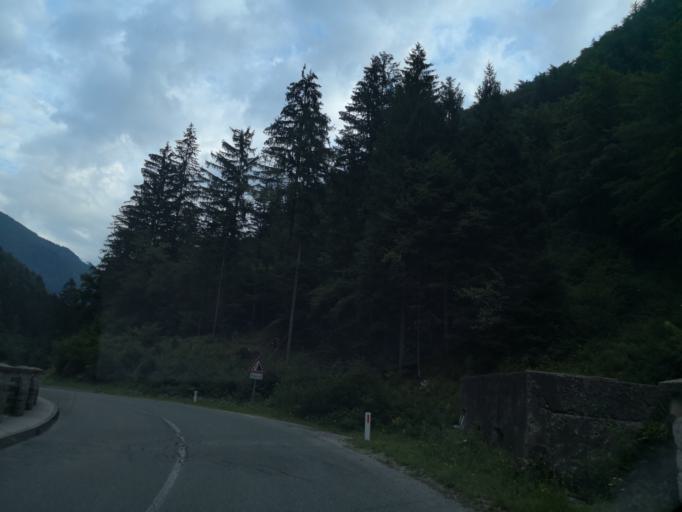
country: SI
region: Jezersko
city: Zgornje Jezersko
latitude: 46.3465
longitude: 14.4814
